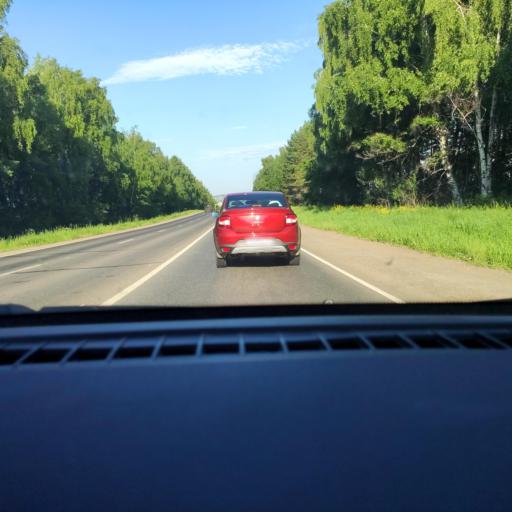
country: RU
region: Udmurtiya
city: Khokhryaki
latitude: 56.9150
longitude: 53.4125
